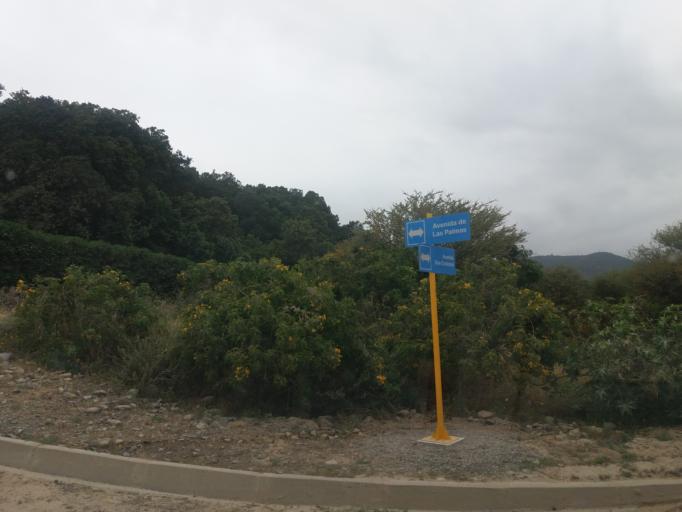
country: CL
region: Valparaiso
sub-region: Provincia de Marga Marga
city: Limache
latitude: -33.0286
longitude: -71.1370
